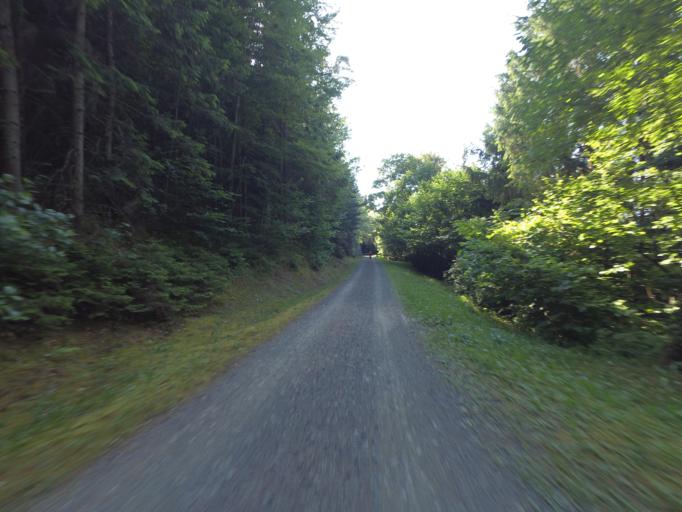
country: AT
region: Carinthia
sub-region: Politischer Bezirk Spittal an der Drau
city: Millstatt
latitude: 46.8003
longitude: 13.5495
